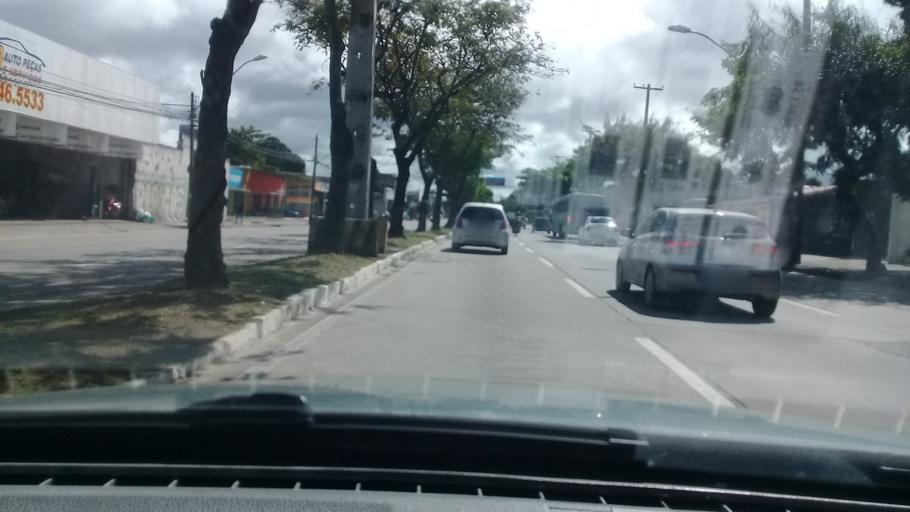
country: BR
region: Pernambuco
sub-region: Recife
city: Recife
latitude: -8.0622
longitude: -34.9189
